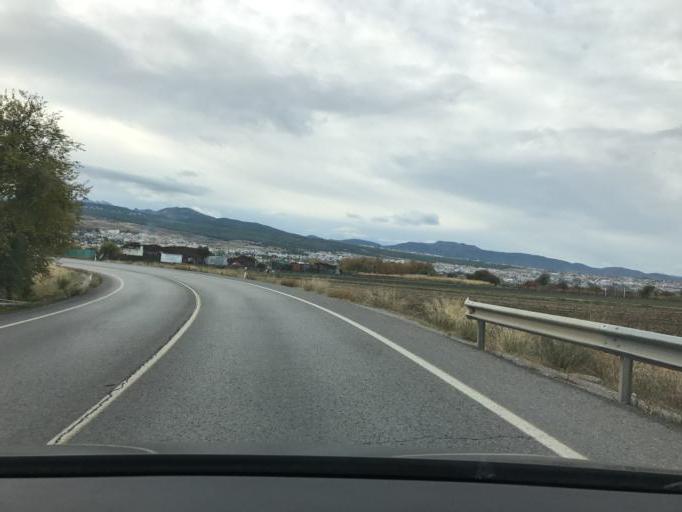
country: ES
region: Andalusia
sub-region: Provincia de Granada
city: Huetor Vega
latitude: 37.1432
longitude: -3.5774
